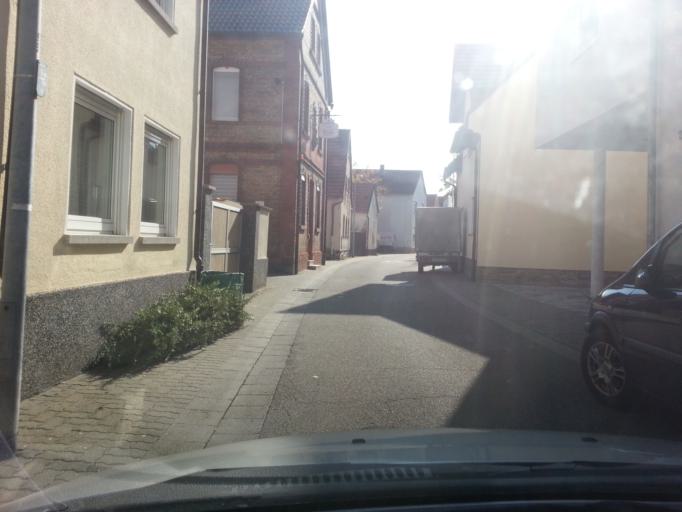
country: DE
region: Rheinland-Pfalz
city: Schifferstadt
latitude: 49.3848
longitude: 8.3721
